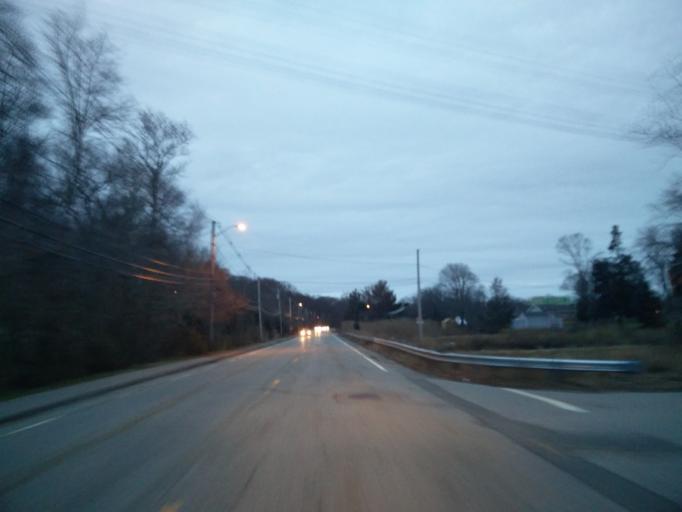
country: US
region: Massachusetts
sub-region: Plymouth County
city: Hingham
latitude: 42.2565
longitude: -70.8503
